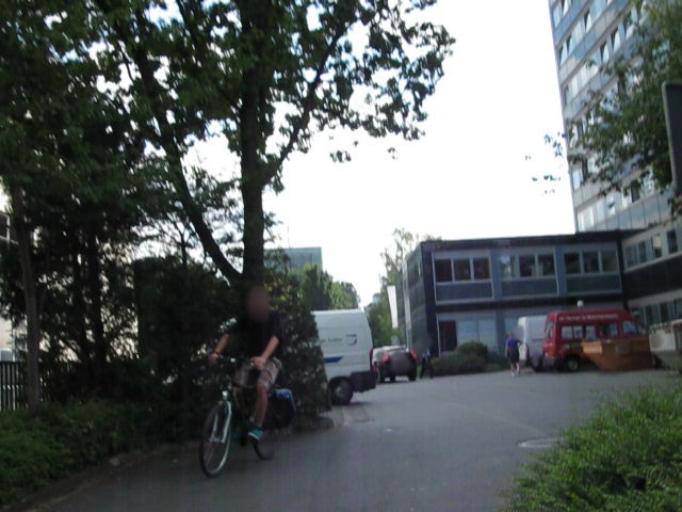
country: DE
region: North Rhine-Westphalia
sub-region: Regierungsbezirk Detmold
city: Paderborn
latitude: 51.7156
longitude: 8.7395
